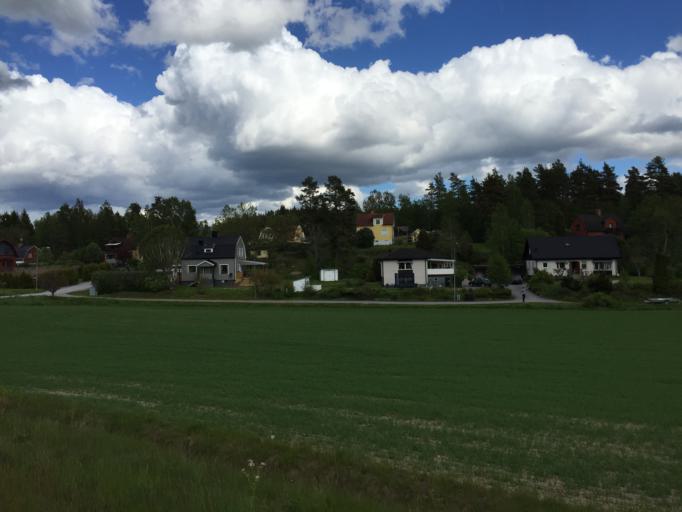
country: SE
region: OEstergoetland
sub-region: Finspangs Kommun
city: Finspang
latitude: 58.6851
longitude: 15.7524
